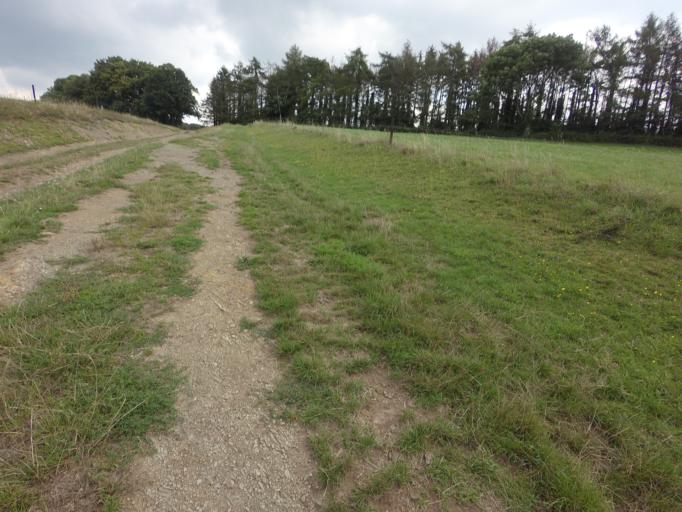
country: BE
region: Wallonia
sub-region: Province de Liege
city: La Calamine
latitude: 50.7069
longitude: 6.0076
